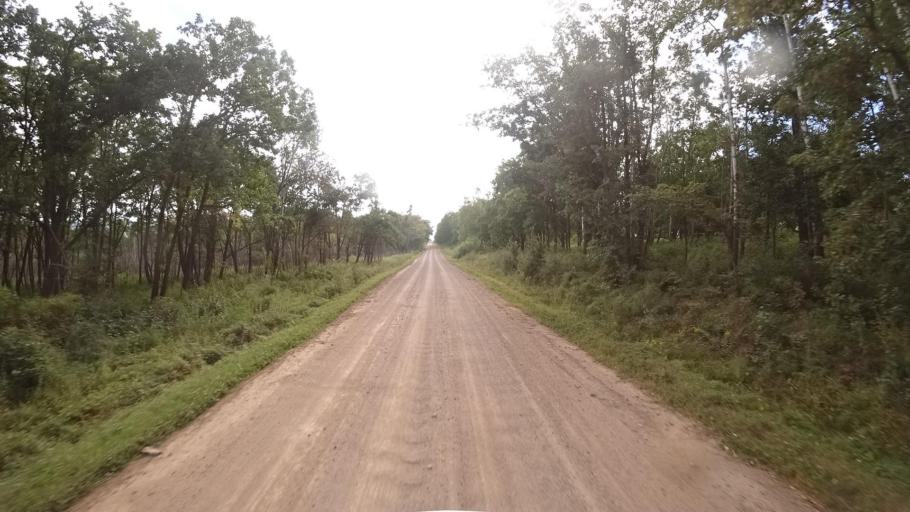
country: RU
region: Primorskiy
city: Dostoyevka
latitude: 44.3458
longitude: 133.5138
